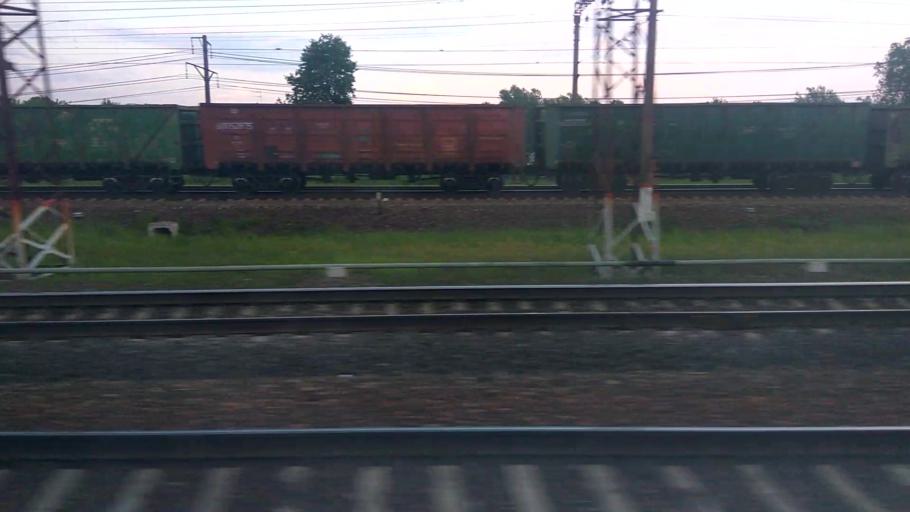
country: RU
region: Moskovskaya
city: Mikhnevo
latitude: 55.1273
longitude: 37.9591
